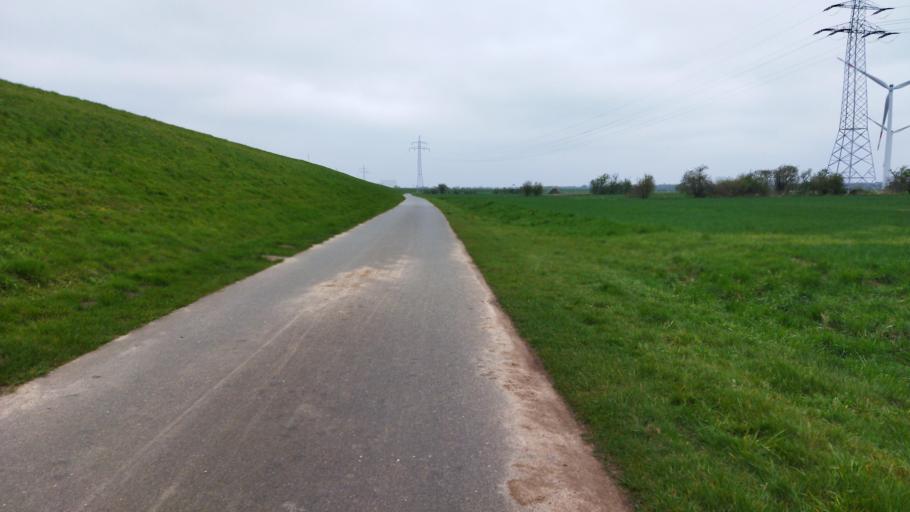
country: DE
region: Lower Saxony
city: Riede
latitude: 53.0188
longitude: 8.9080
